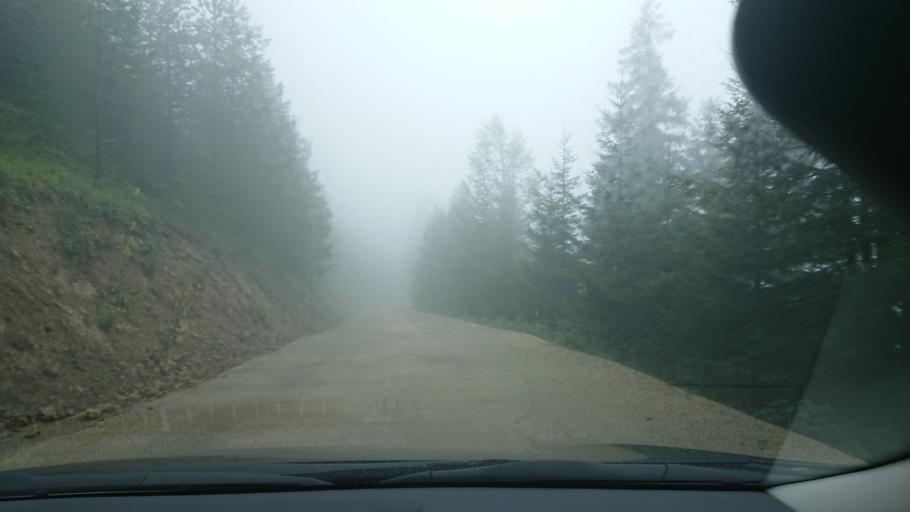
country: TR
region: Gumushane
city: Kurtun
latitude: 40.6629
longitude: 39.0148
